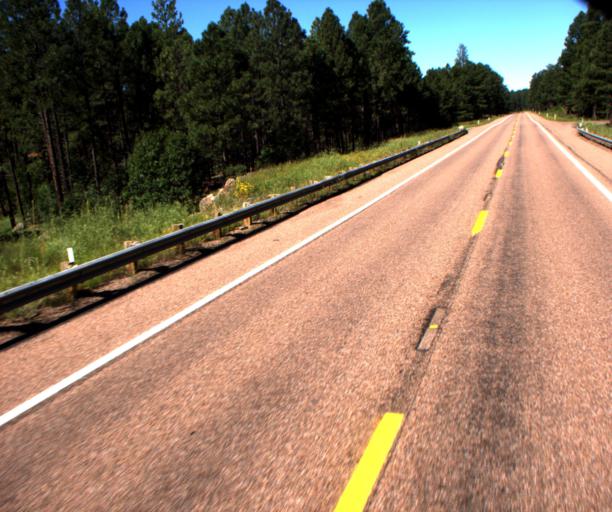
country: US
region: Arizona
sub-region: Navajo County
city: Pinetop-Lakeside
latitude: 34.0796
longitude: -109.8096
